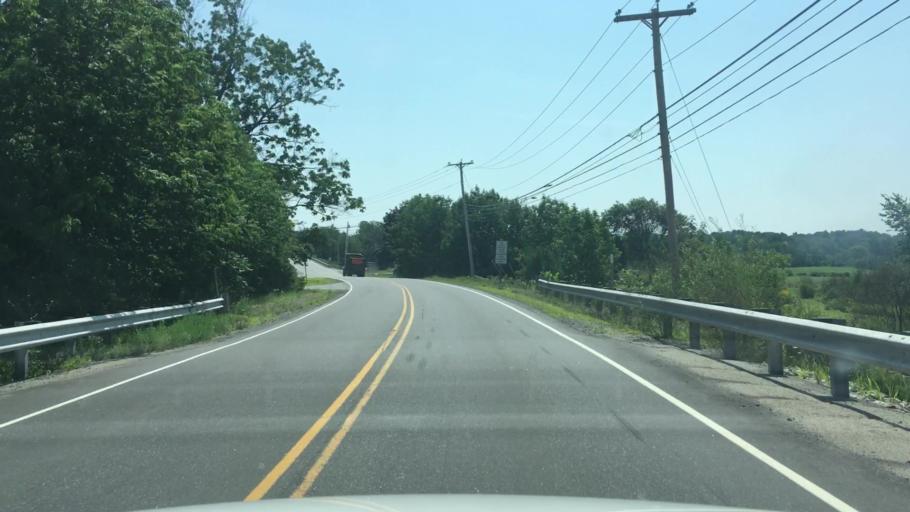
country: US
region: Maine
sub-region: Kennebec County
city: Hallowell
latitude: 44.2990
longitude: -69.8113
